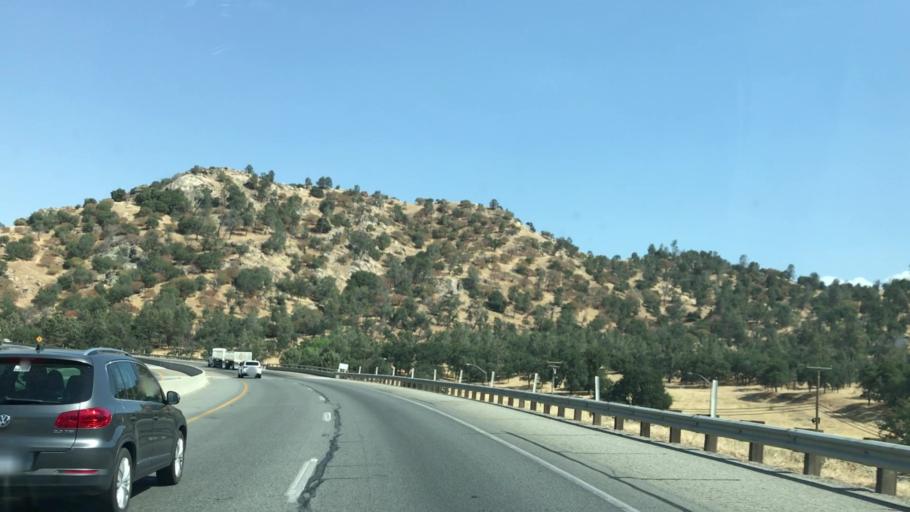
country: US
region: California
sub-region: Kern County
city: Bear Valley Springs
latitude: 35.2242
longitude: -118.5678
